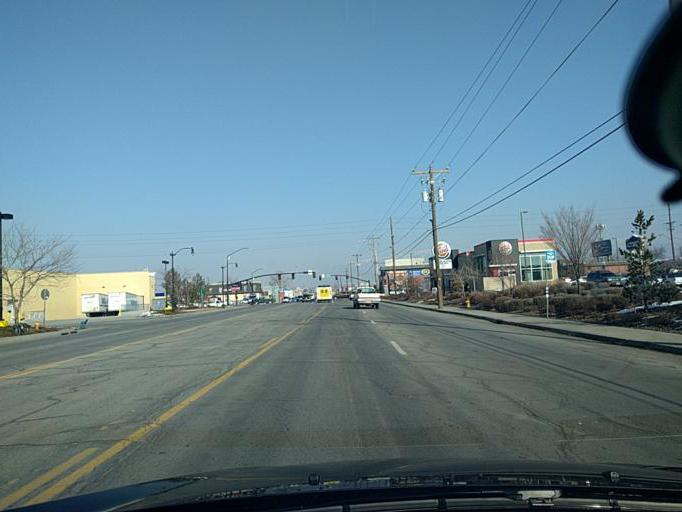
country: US
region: Utah
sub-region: Salt Lake County
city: Salt Lake City
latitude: 40.7404
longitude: -111.8996
